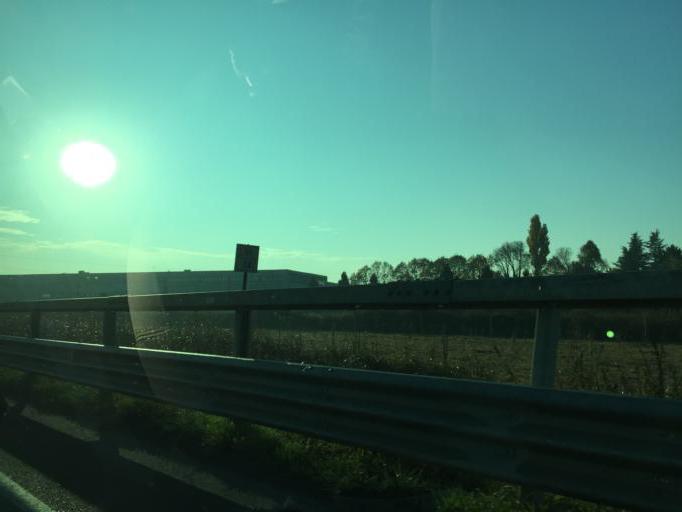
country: IT
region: Lombardy
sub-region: Citta metropolitana di Milano
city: Melzo
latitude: 45.4813
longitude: 9.4352
